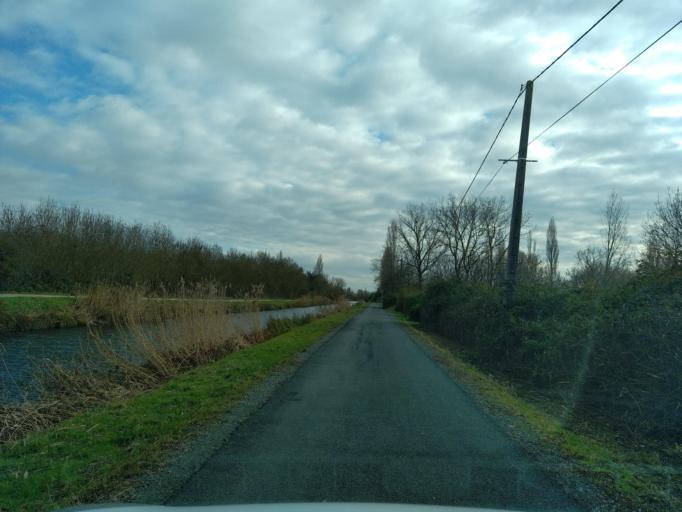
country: FR
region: Pays de la Loire
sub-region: Departement de la Vendee
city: Maillezais
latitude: 46.3160
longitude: -0.7752
